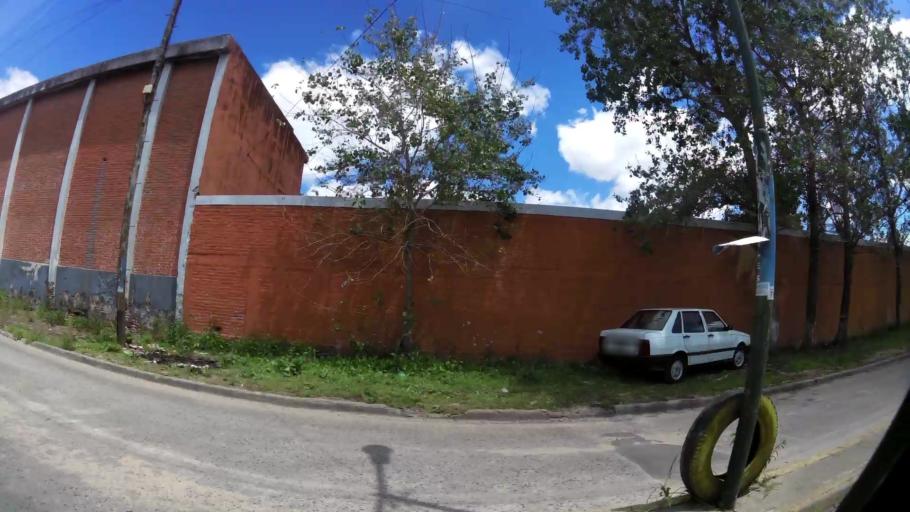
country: AR
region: Buenos Aires
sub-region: Partido de Lanus
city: Lanus
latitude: -34.7221
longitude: -58.4215
